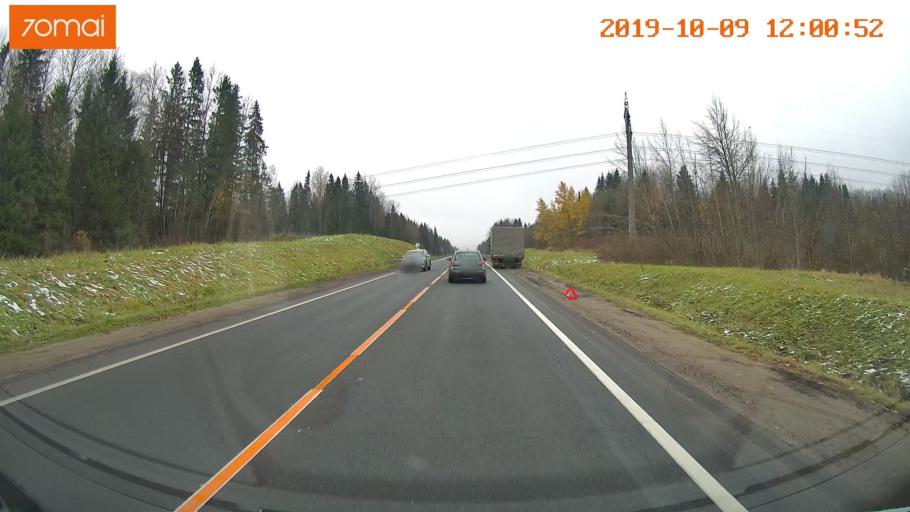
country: RU
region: Vologda
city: Gryazovets
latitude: 58.6938
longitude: 40.3010
